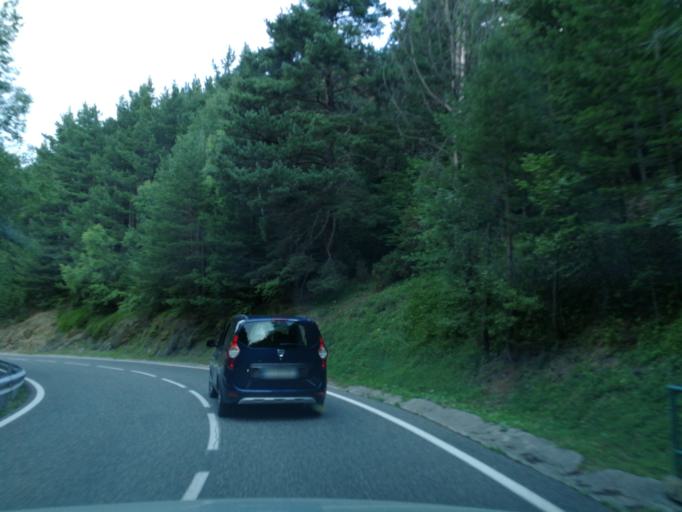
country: AD
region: Ordino
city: Ordino
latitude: 42.5532
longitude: 1.5445
